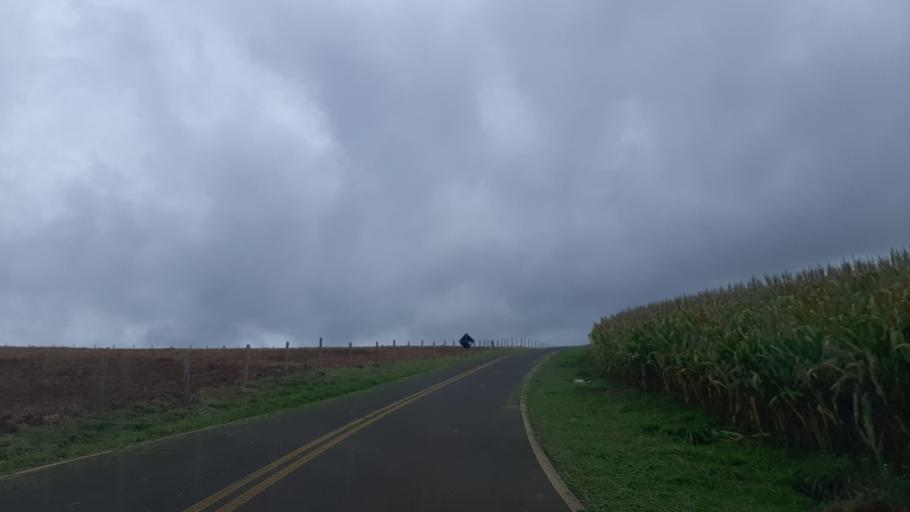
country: BR
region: Parana
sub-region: Ampere
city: Ampere
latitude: -25.9477
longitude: -53.4585
